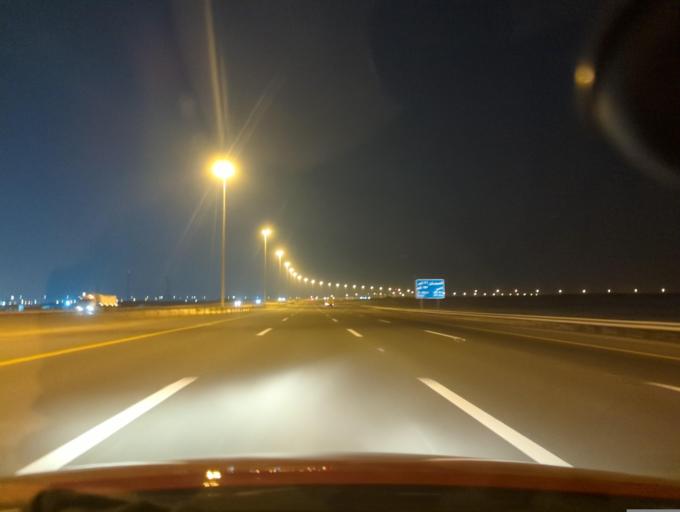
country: AE
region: Abu Dhabi
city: Abu Dhabi
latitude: 24.4417
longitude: 54.7587
